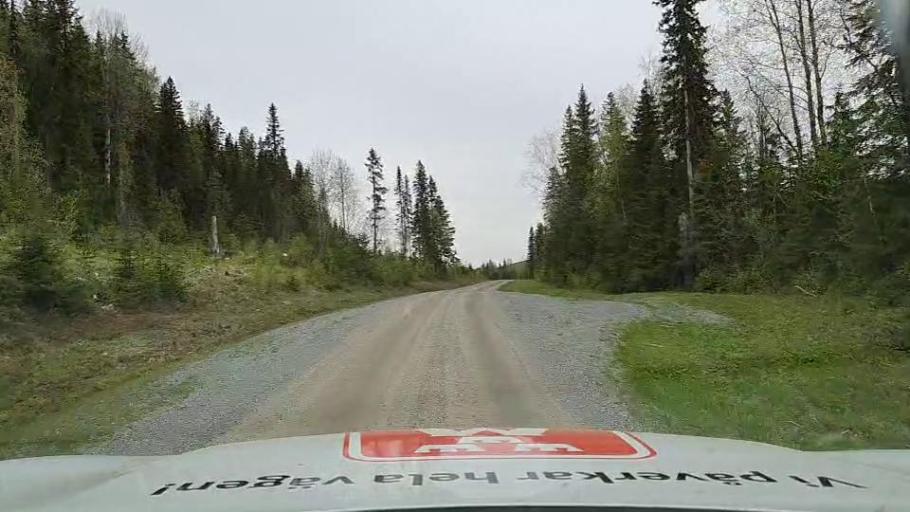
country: SE
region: Jaemtland
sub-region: Bergs Kommun
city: Hoverberg
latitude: 62.5438
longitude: 14.6982
